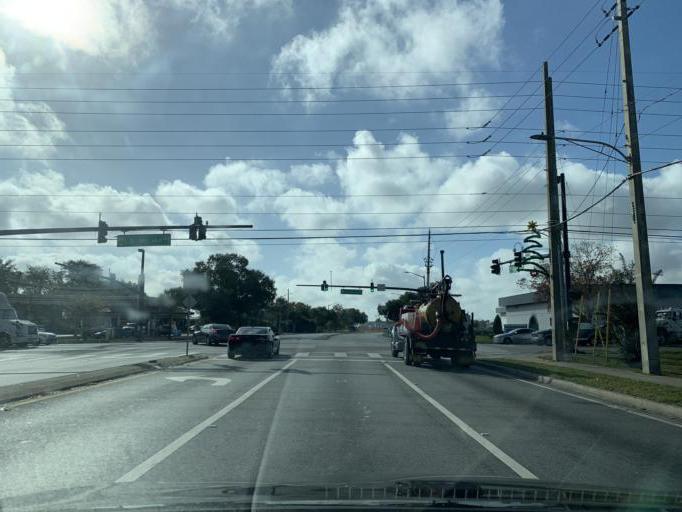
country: US
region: Florida
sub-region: Orange County
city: Oak Ridge
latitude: 28.5092
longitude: -81.4260
